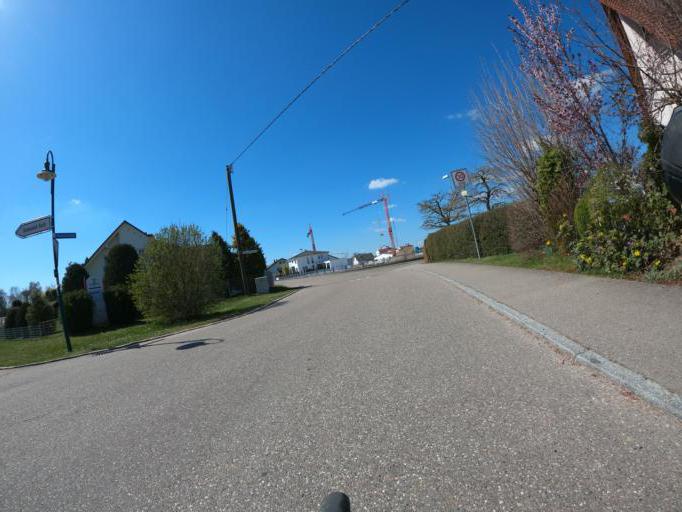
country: DE
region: Baden-Wuerttemberg
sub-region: Karlsruhe Region
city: Horb am Neckar
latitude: 48.4336
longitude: 8.6997
